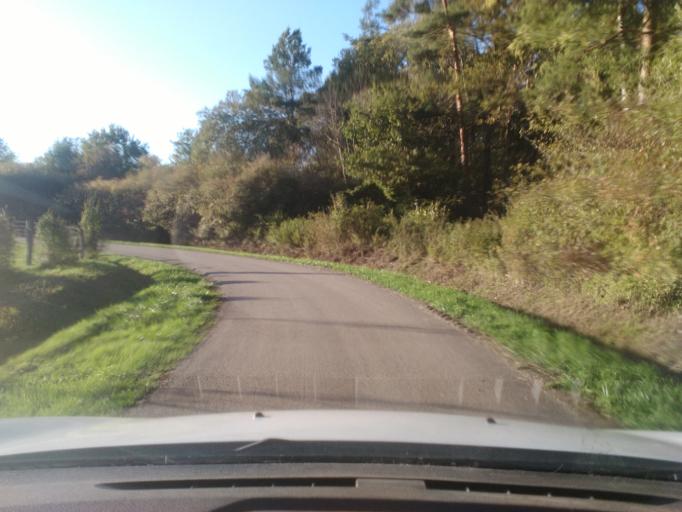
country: FR
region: Lorraine
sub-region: Departement des Vosges
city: Rambervillers
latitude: 48.2888
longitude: 6.6364
